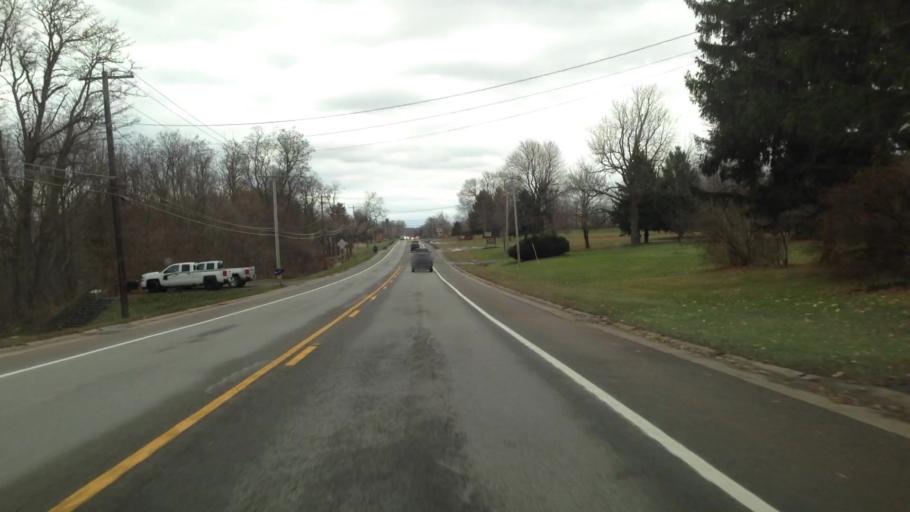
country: US
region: New York
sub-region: Erie County
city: Clarence
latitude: 42.9918
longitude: -78.5500
